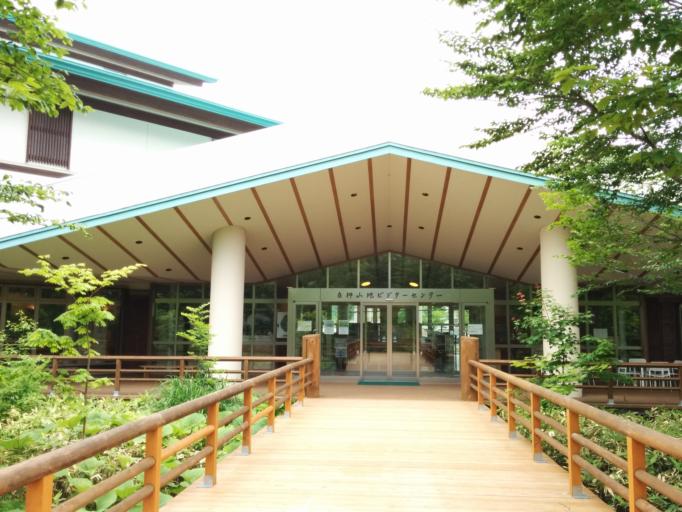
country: JP
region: Aomori
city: Hirosaki
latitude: 40.5786
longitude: 140.2988
